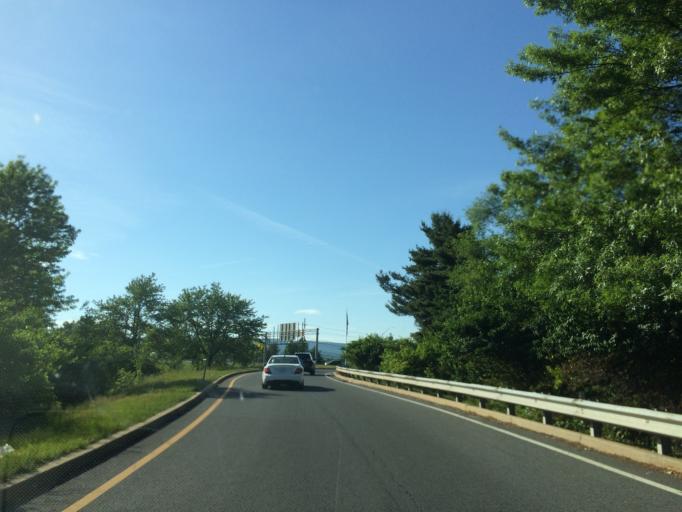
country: US
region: Maryland
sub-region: Frederick County
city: Frederick
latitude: 39.4165
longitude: -77.4331
